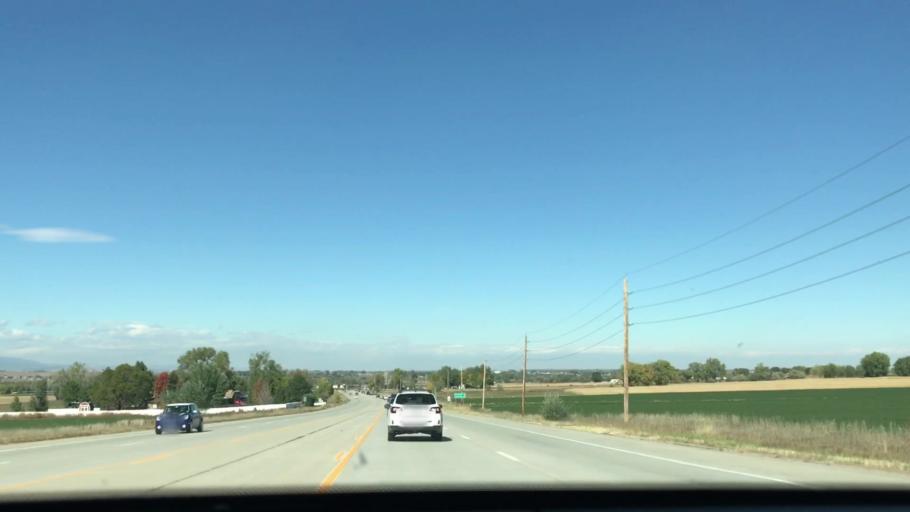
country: US
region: Colorado
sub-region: Boulder County
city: Lafayette
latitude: 40.0257
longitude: -105.1026
